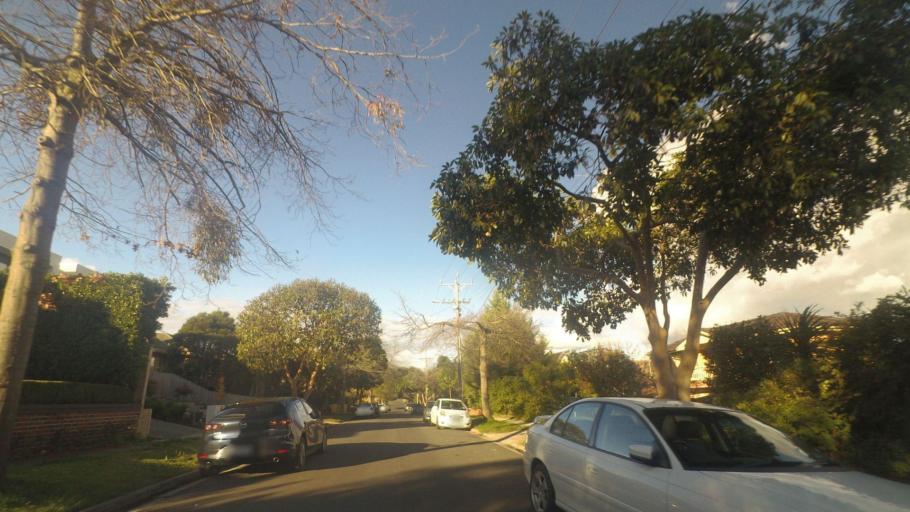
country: AU
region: Victoria
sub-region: Manningham
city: Templestowe Lower
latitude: -37.7742
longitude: 145.1098
